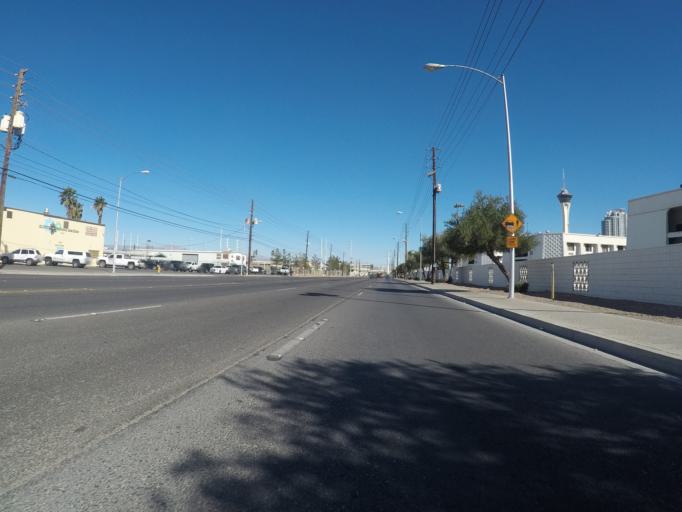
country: US
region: Nevada
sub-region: Clark County
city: Las Vegas
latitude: 36.1403
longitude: -115.1671
